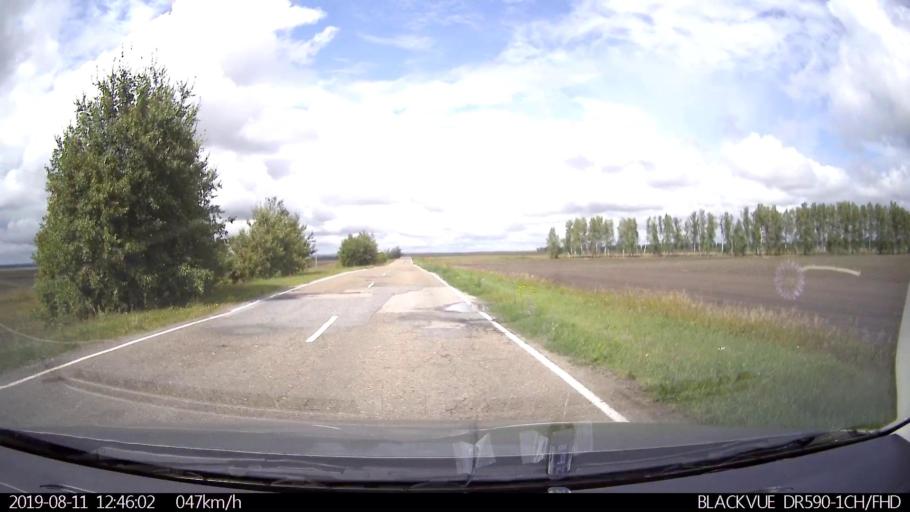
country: RU
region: Ulyanovsk
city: Ignatovka
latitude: 53.8622
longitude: 47.7227
